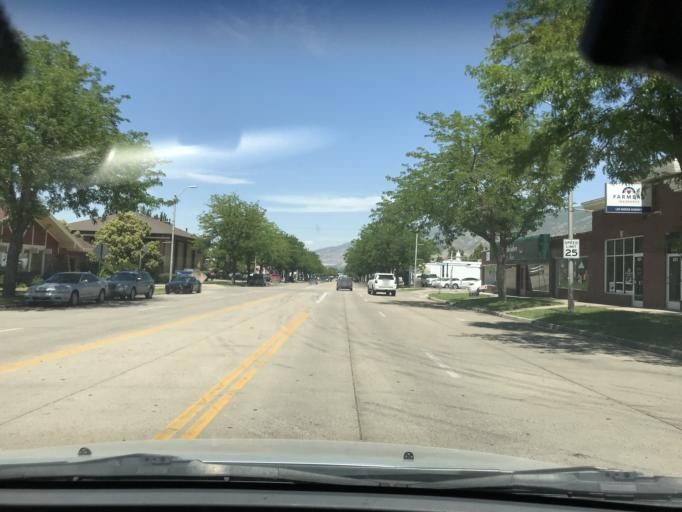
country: US
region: Utah
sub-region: Davis County
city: Bountiful
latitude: 40.8846
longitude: -111.8807
